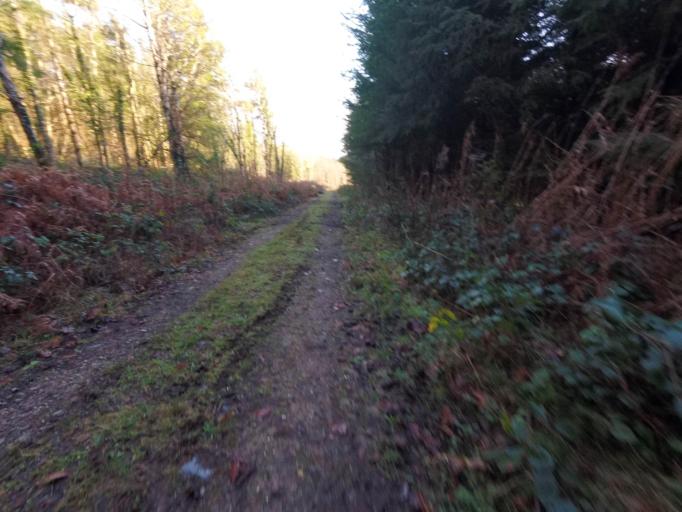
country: IE
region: Munster
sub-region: Waterford
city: Portlaw
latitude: 52.3052
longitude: -7.3529
